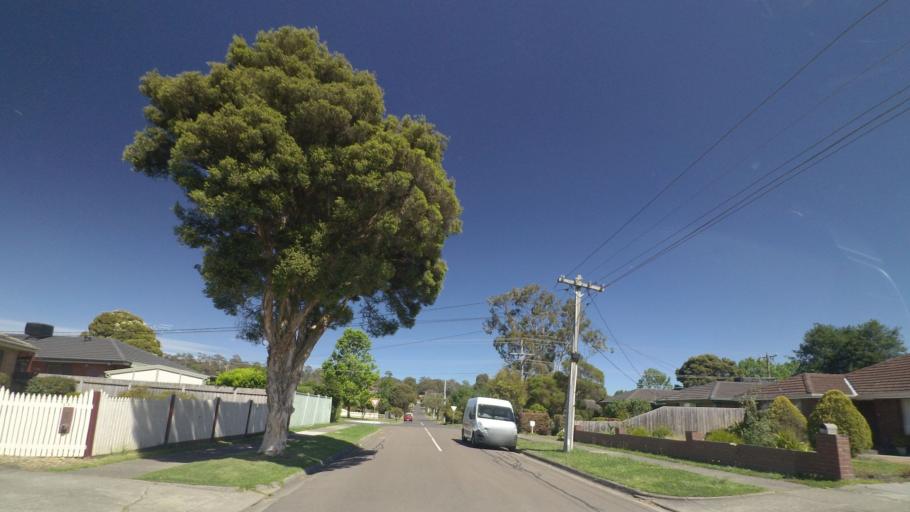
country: AU
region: Victoria
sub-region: Yarra Ranges
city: Kilsyth
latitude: -37.7990
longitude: 145.3195
